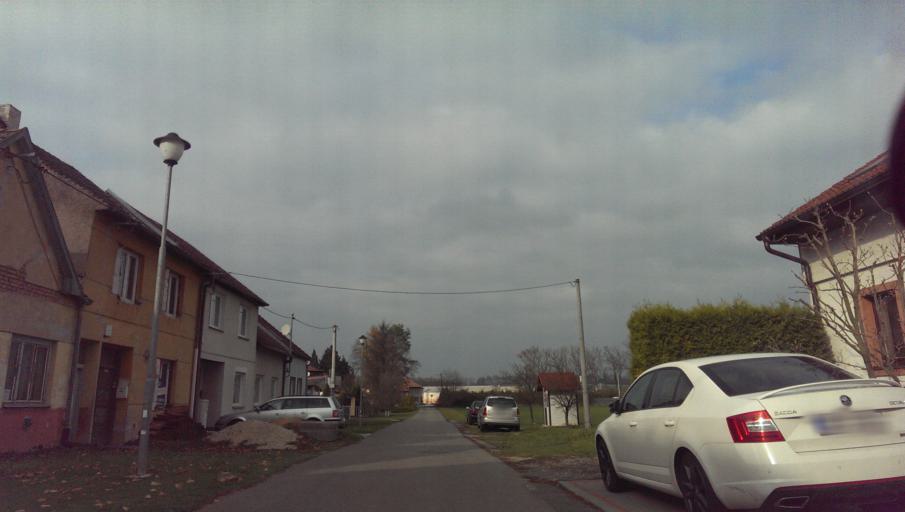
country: CZ
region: Zlin
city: Tlumacov
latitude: 49.2593
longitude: 17.5015
